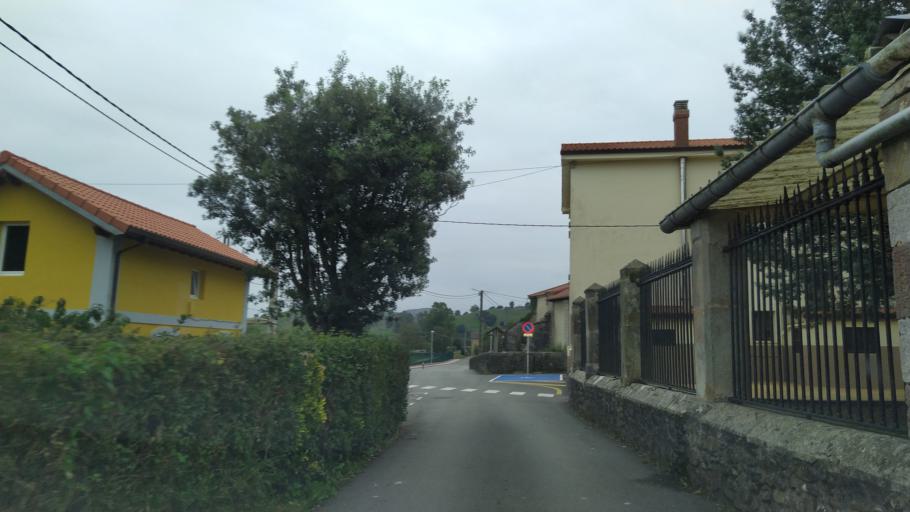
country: ES
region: Cantabria
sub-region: Provincia de Cantabria
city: Entrambasaguas
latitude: 43.3765
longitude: -3.7184
